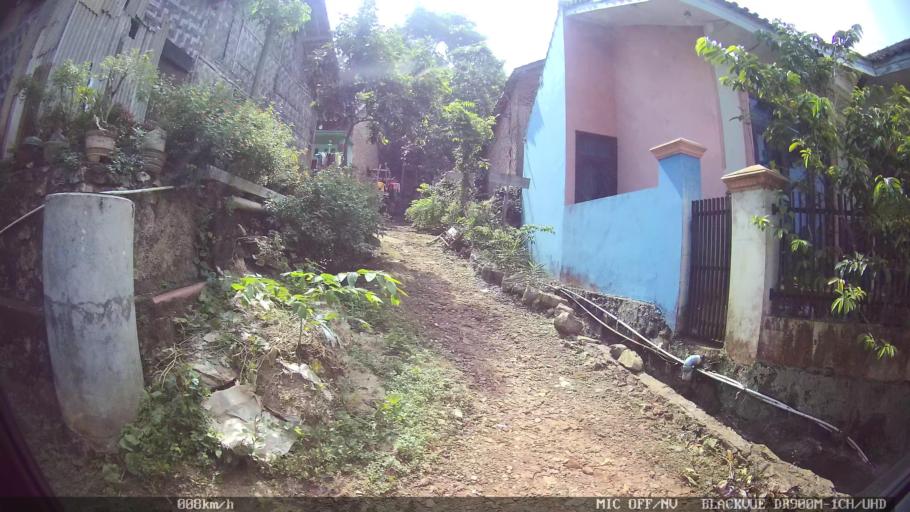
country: ID
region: Lampung
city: Kedaton
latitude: -5.3971
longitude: 105.2280
